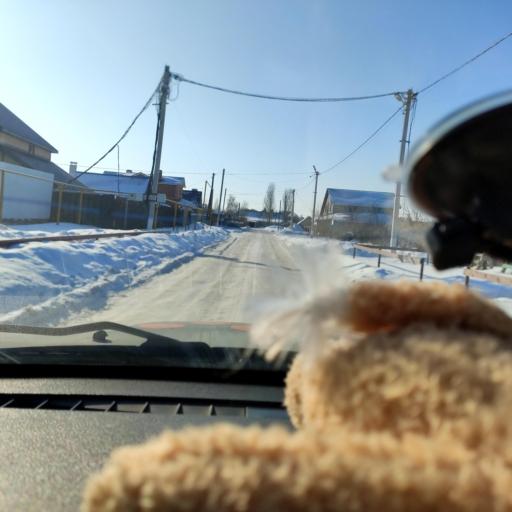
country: RU
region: Samara
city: Podstepki
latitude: 53.5153
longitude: 49.1244
